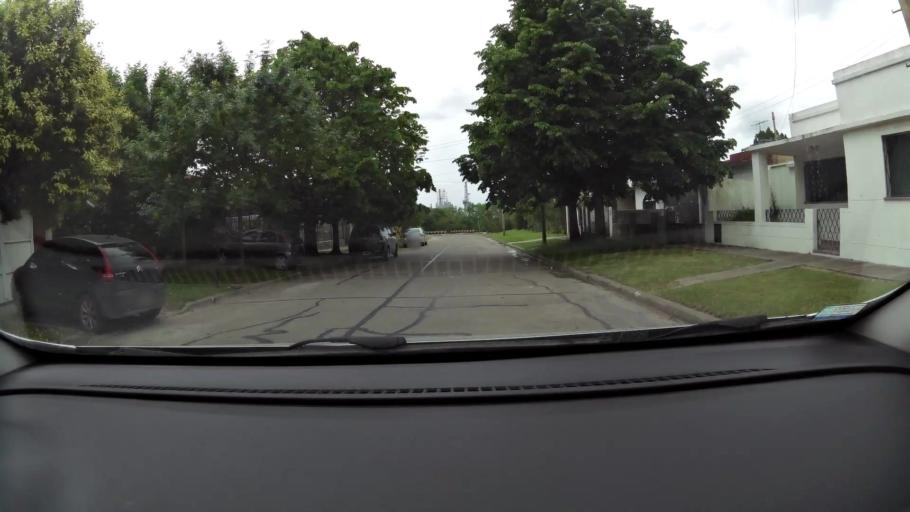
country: AR
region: Buenos Aires
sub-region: Partido de Campana
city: Campana
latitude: -34.1645
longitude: -58.9513
